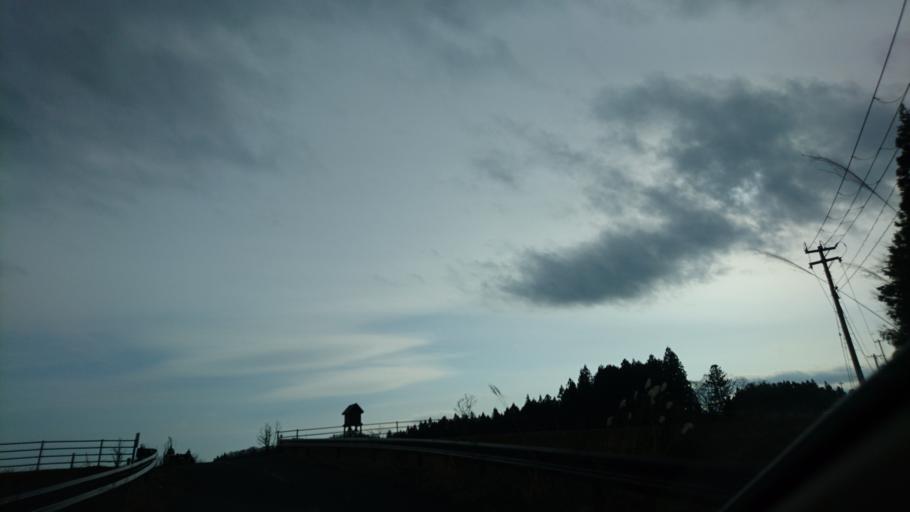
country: JP
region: Iwate
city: Ichinoseki
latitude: 38.9417
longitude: 141.0767
